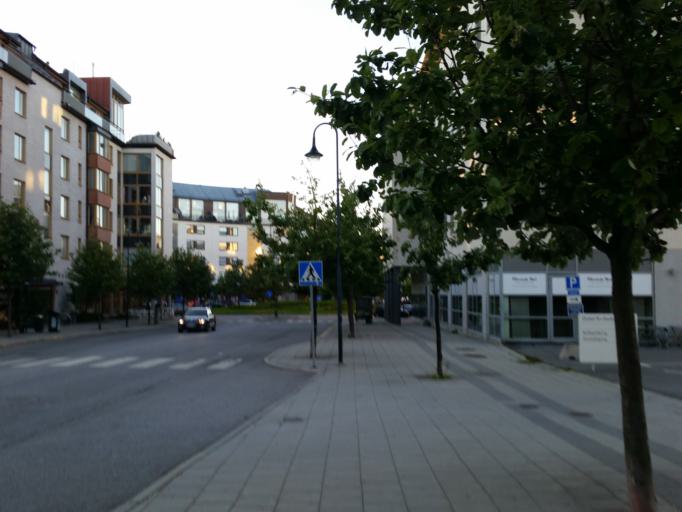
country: SE
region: Stockholm
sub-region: Solna Kommun
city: Solna
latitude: 59.3708
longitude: 18.0170
